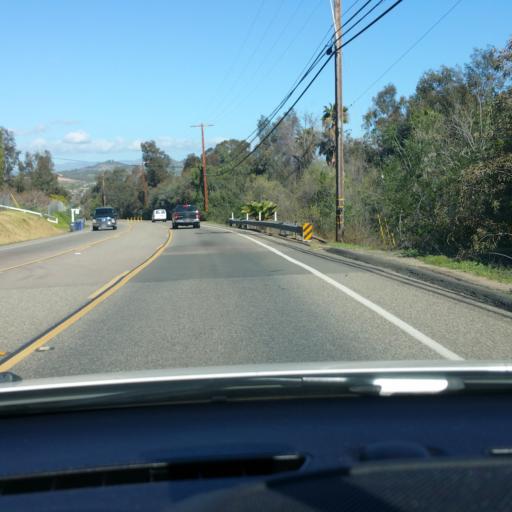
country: US
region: California
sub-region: San Diego County
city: Bonsall
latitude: 33.2517
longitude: -117.2311
